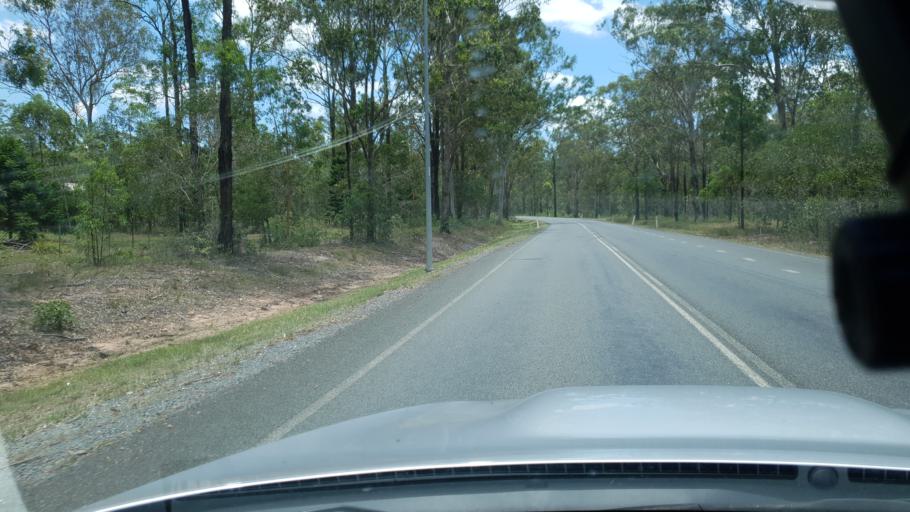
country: AU
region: Queensland
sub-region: Logan
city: North Maclean
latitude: -27.7604
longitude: 152.9868
